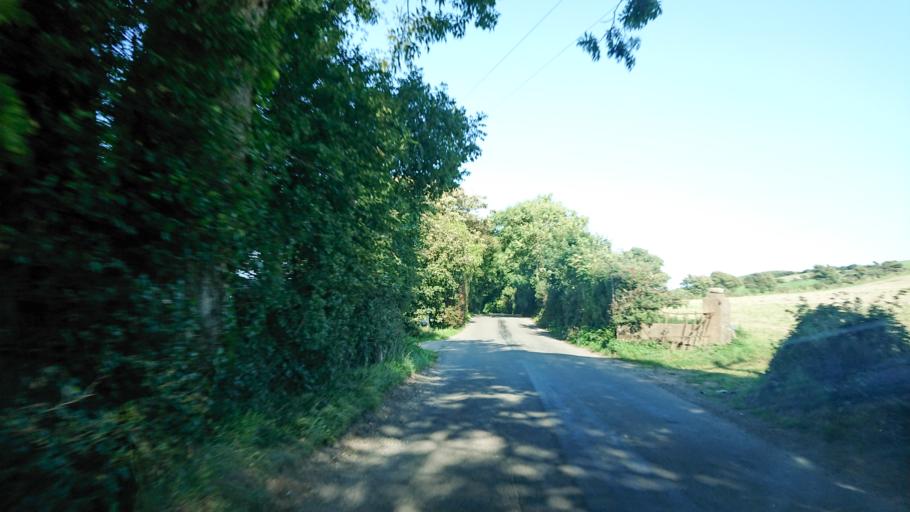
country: IE
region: Munster
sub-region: Waterford
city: Dunmore East
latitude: 52.1850
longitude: -7.0012
